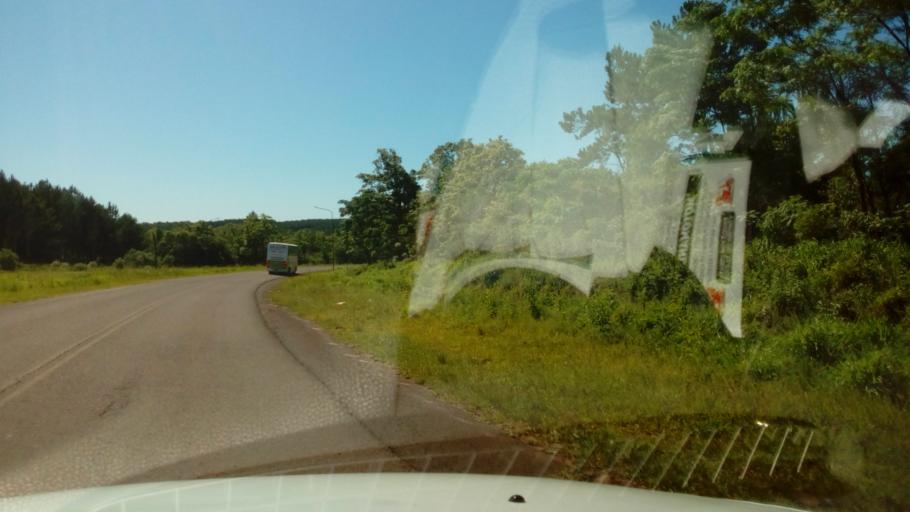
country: AR
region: Misiones
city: Santa Ana
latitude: -27.4151
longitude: -55.5242
